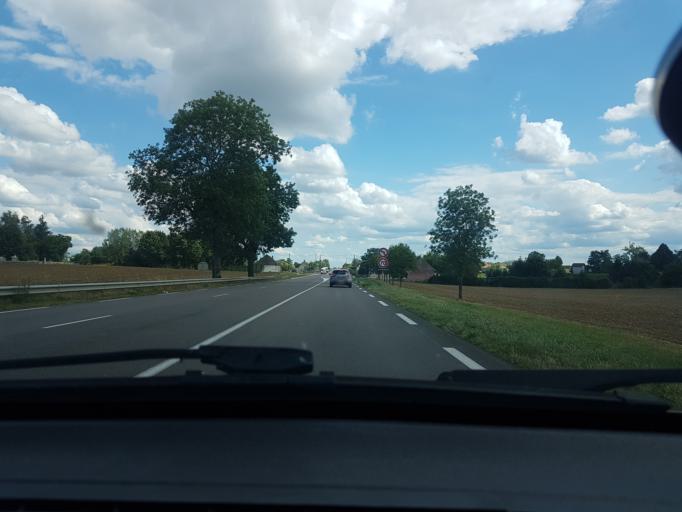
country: FR
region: Bourgogne
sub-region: Departement de Saone-et-Loire
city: Fontaines
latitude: 46.8497
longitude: 4.8074
